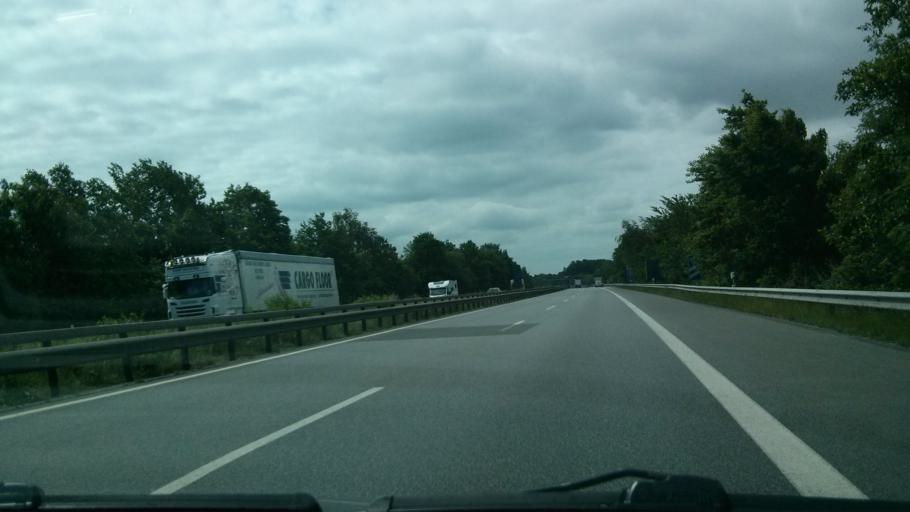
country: DE
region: Lower Saxony
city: Loxstedt
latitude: 53.4486
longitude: 8.5863
